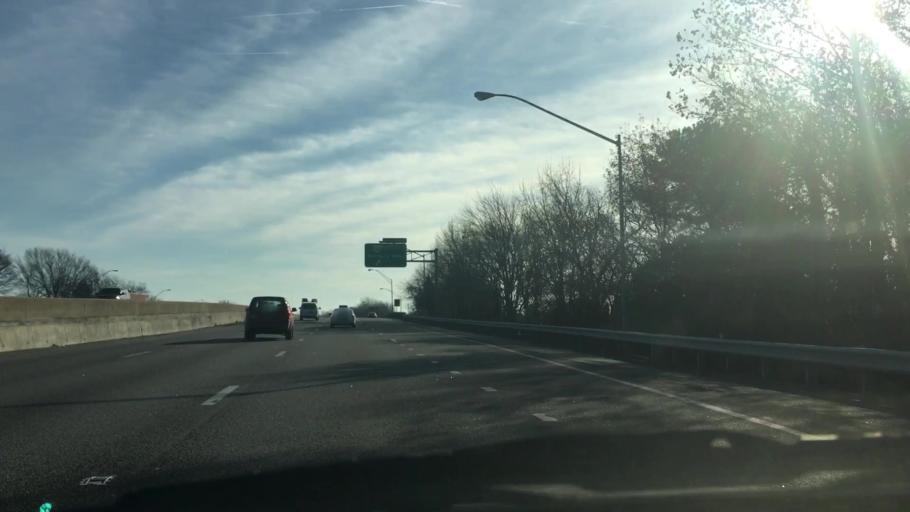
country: US
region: Virginia
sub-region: City of Norfolk
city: Norfolk
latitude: 36.8826
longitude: -76.2174
